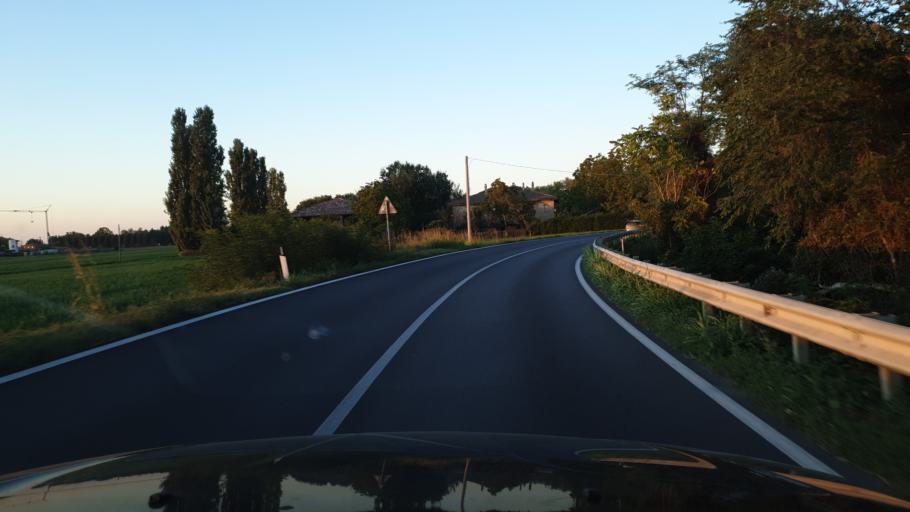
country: IT
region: Emilia-Romagna
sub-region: Provincia di Bologna
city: Progresso
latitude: 44.5525
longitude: 11.3880
